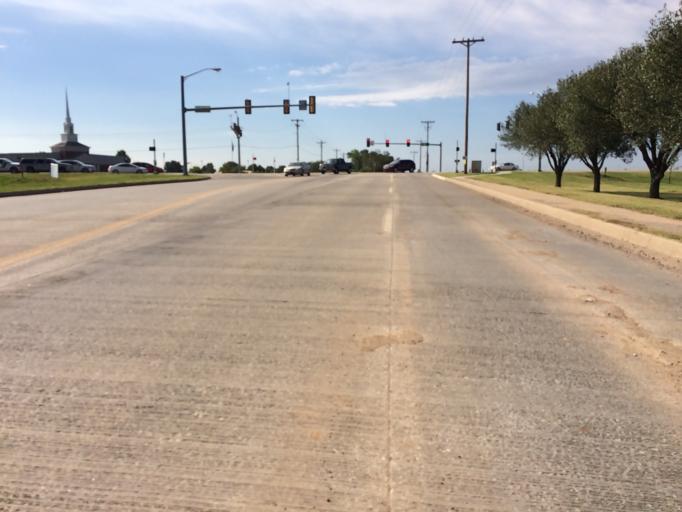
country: US
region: Oklahoma
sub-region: Cleveland County
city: Norman
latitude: 35.1894
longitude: -97.4059
